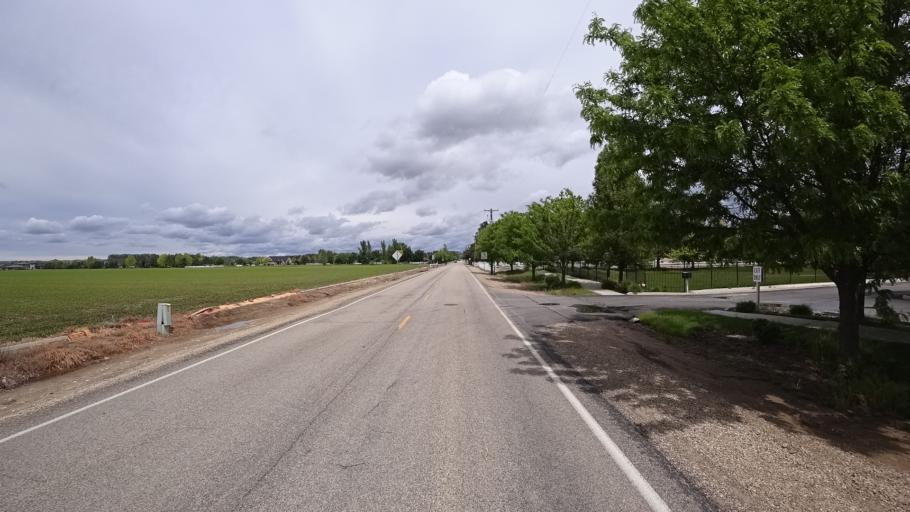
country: US
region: Idaho
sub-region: Ada County
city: Eagle
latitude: 43.7076
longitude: -116.4037
